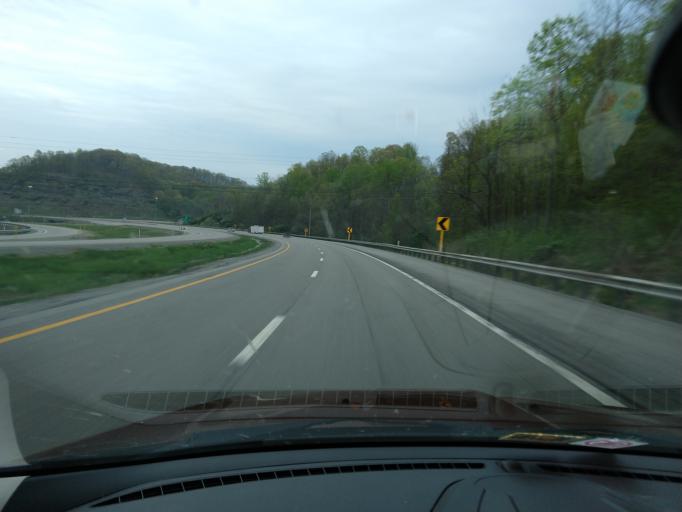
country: US
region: West Virginia
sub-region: Lewis County
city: Weston
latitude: 38.9605
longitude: -80.5192
